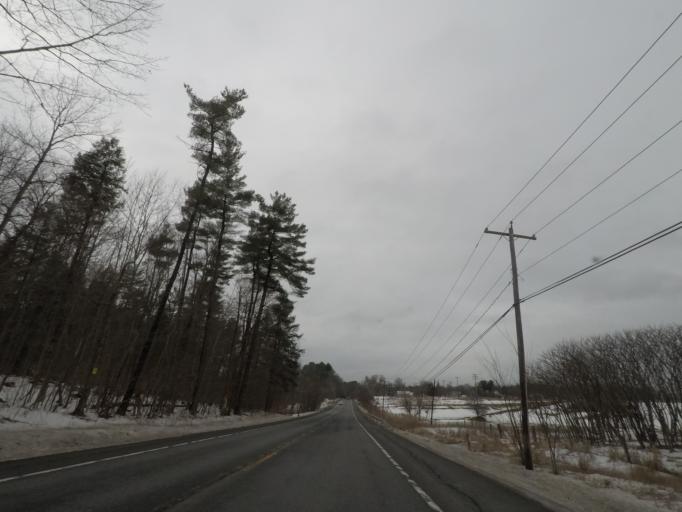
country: US
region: New York
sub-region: Schenectady County
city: Rotterdam
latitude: 42.7282
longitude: -73.9676
